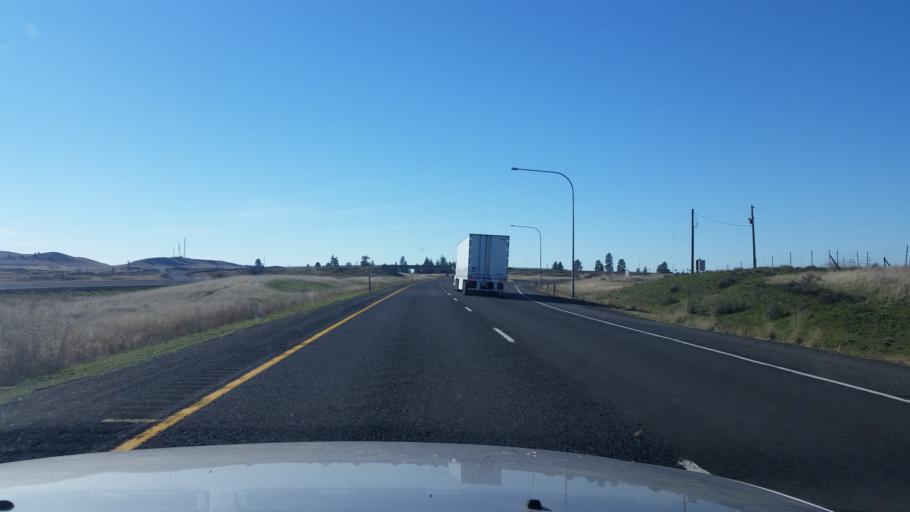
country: US
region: Washington
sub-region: Spokane County
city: Medical Lake
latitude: 47.3992
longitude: -117.8366
